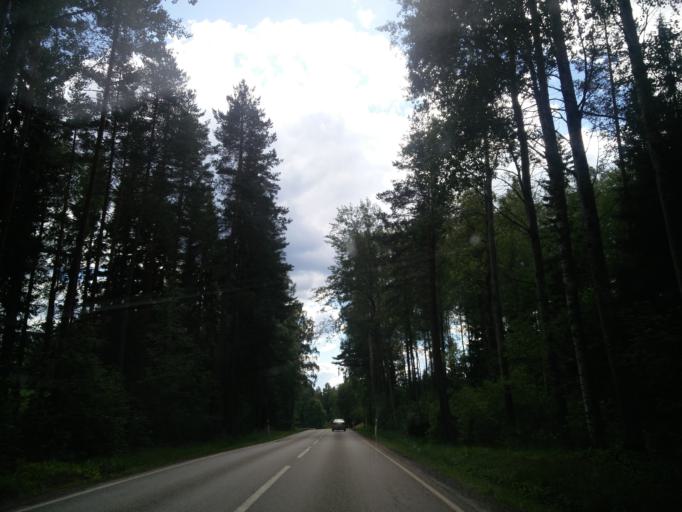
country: SE
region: OErebro
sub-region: Ljusnarsbergs Kommun
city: Kopparberg
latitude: 59.8555
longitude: 15.0003
